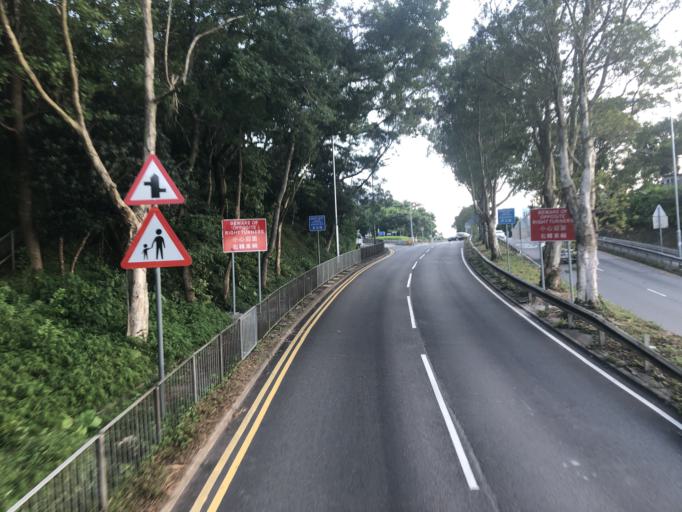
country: HK
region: Sai Kung
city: Sai Kung
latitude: 22.3409
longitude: 114.2481
